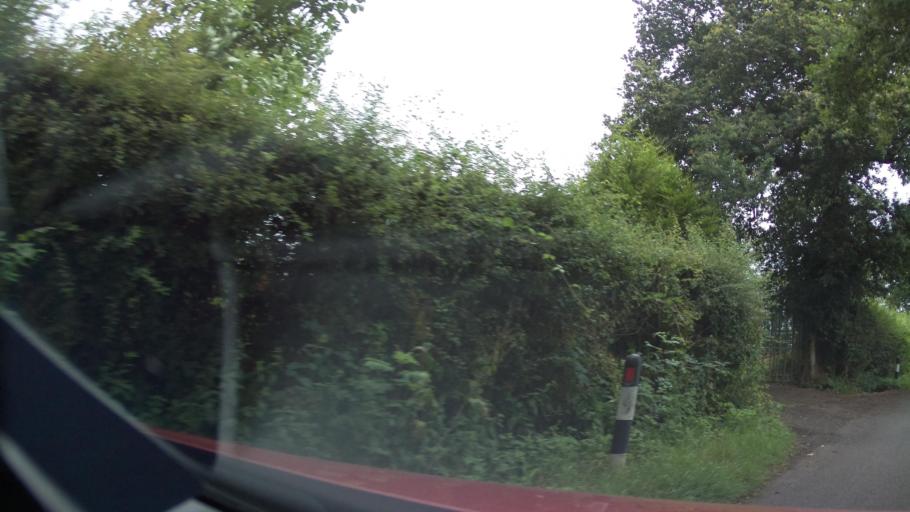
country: GB
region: England
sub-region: Solihull
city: Dickens Heath
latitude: 52.3736
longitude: -1.8373
